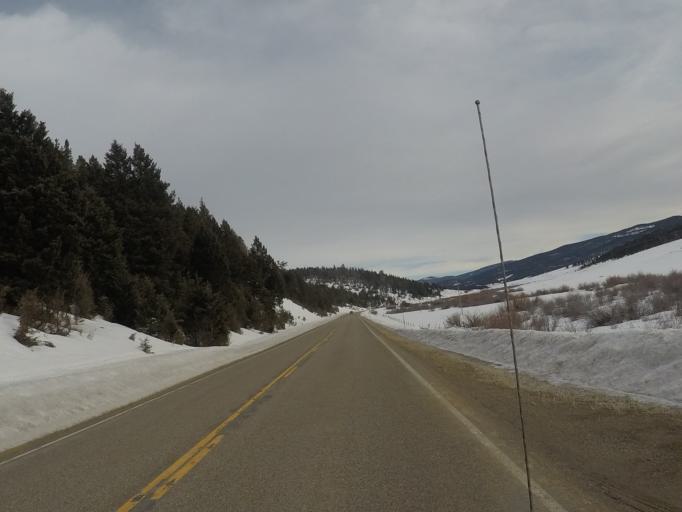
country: US
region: Montana
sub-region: Meagher County
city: White Sulphur Springs
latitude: 46.7013
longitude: -110.8625
